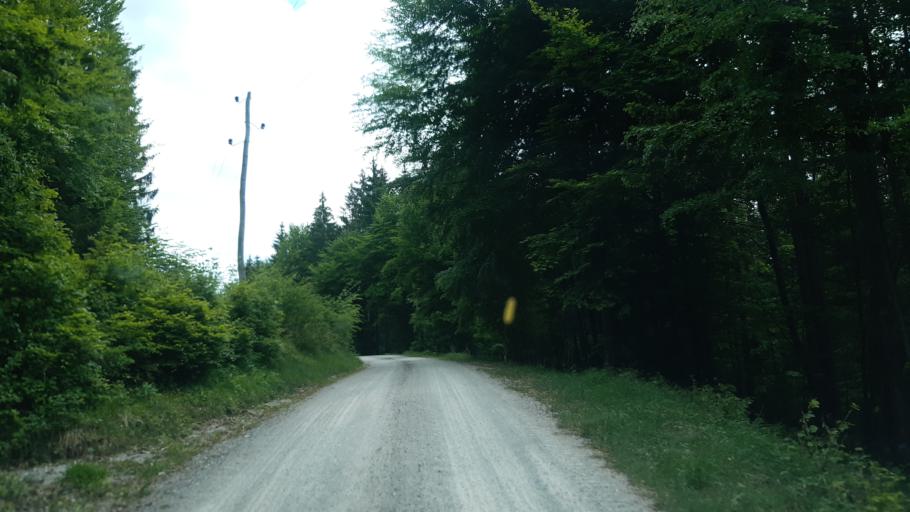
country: SI
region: Kocevje
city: Kocevje
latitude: 45.6315
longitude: 14.9994
